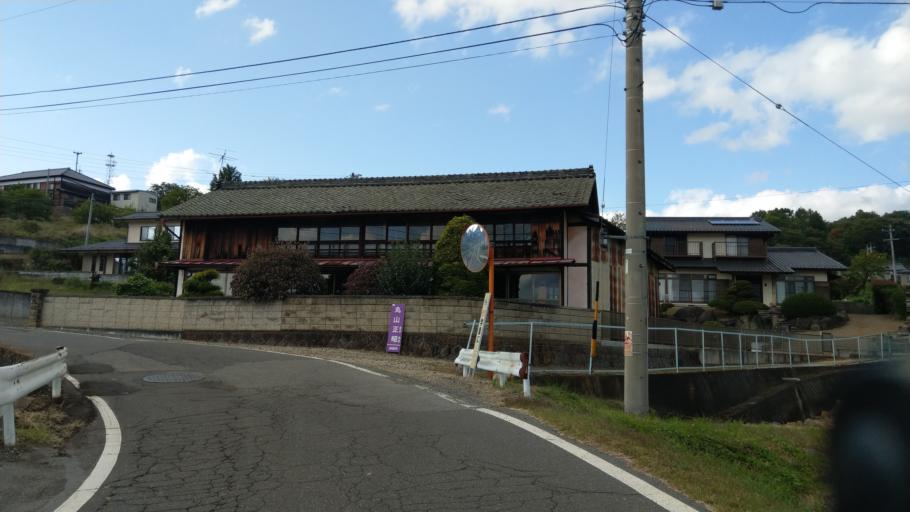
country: JP
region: Nagano
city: Komoro
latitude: 36.3488
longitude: 138.4125
